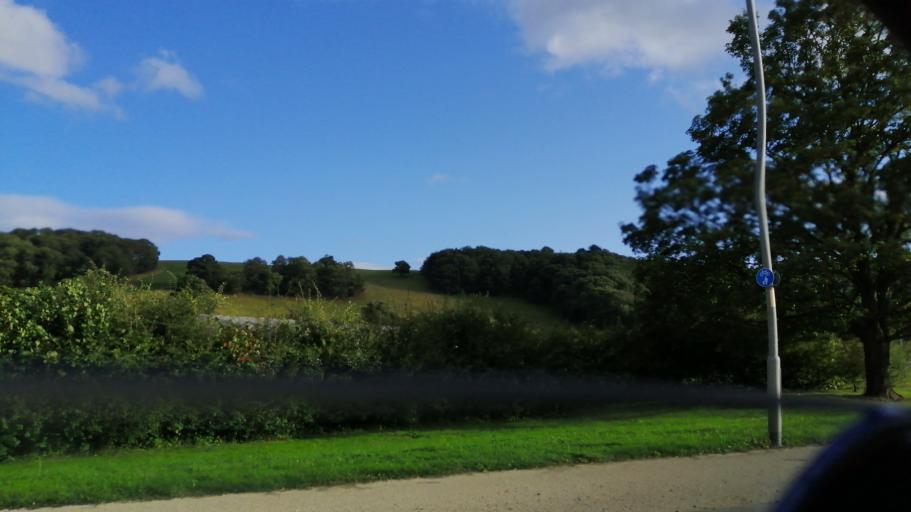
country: GB
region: England
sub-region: Herefordshire
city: Lower Bullingham
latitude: 52.0375
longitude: -2.6821
